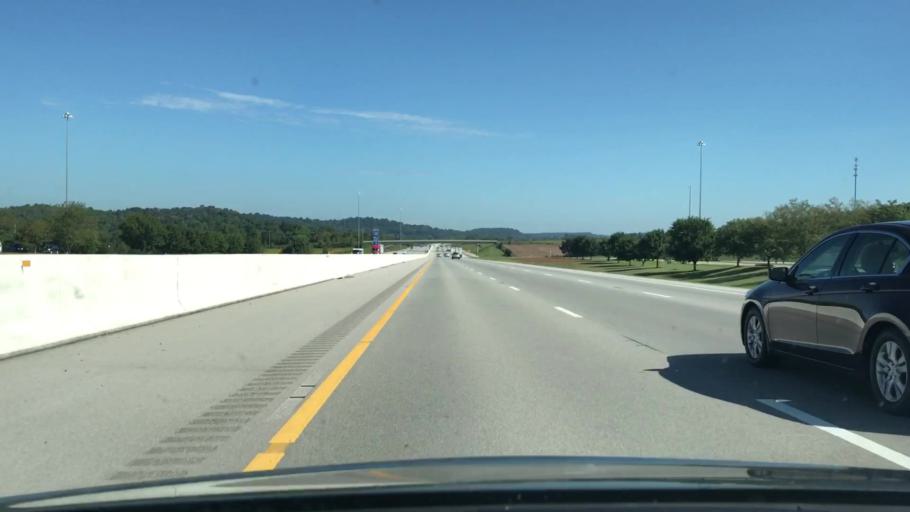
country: US
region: Kentucky
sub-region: Hart County
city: Munfordville
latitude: 37.2386
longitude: -85.9283
